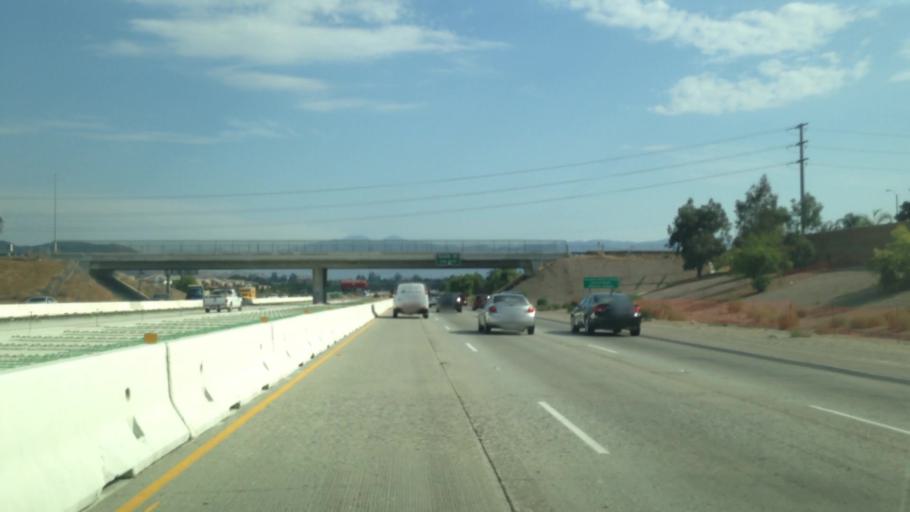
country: US
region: California
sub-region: Riverside County
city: Norco
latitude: 33.9659
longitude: -117.5490
